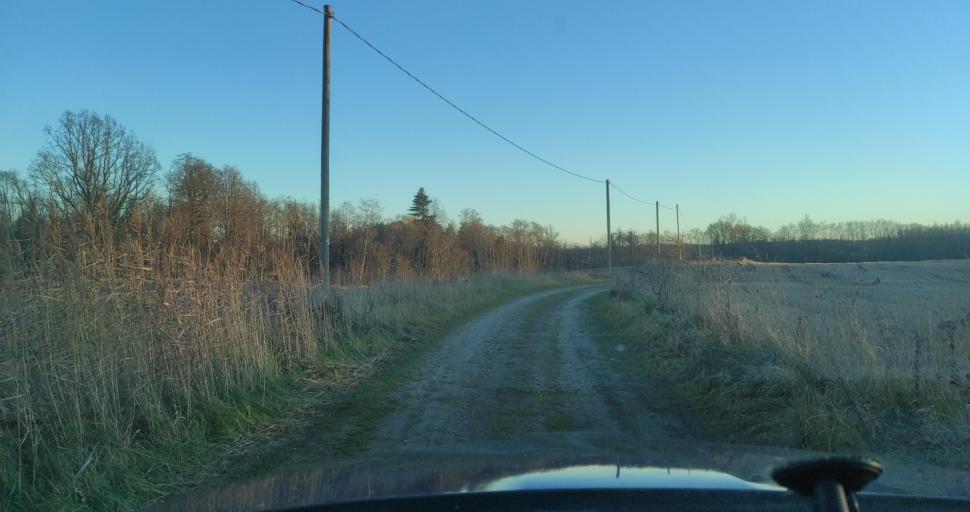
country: LV
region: Dundaga
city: Dundaga
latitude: 57.3934
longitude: 22.0867
